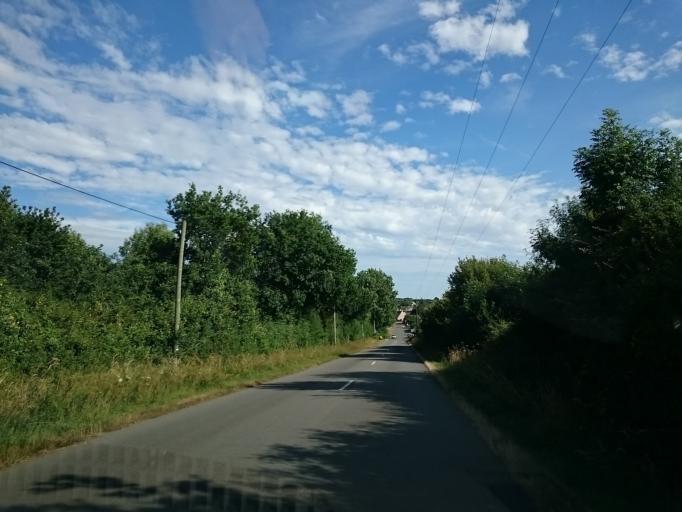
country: FR
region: Brittany
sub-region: Departement d'Ille-et-Vilaine
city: Pance
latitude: 47.9004
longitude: -1.6152
